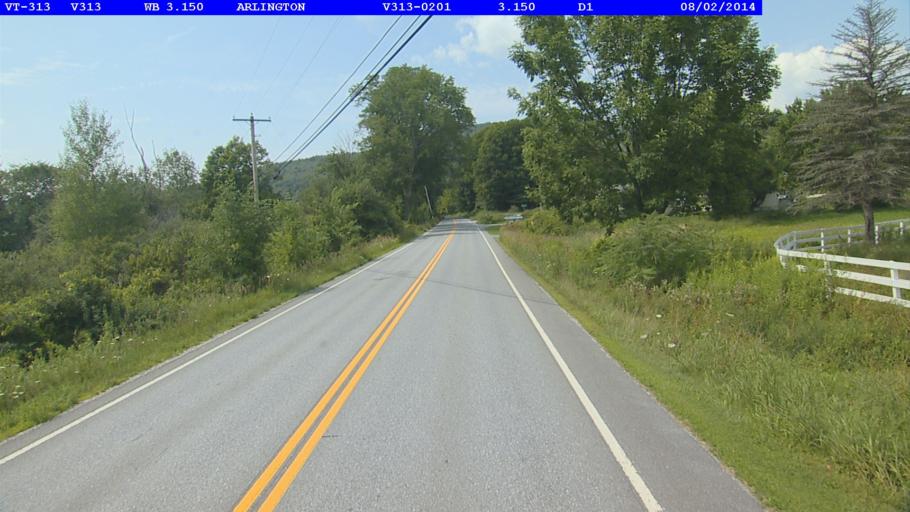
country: US
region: Vermont
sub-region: Bennington County
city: Arlington
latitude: 43.1009
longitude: -73.2075
